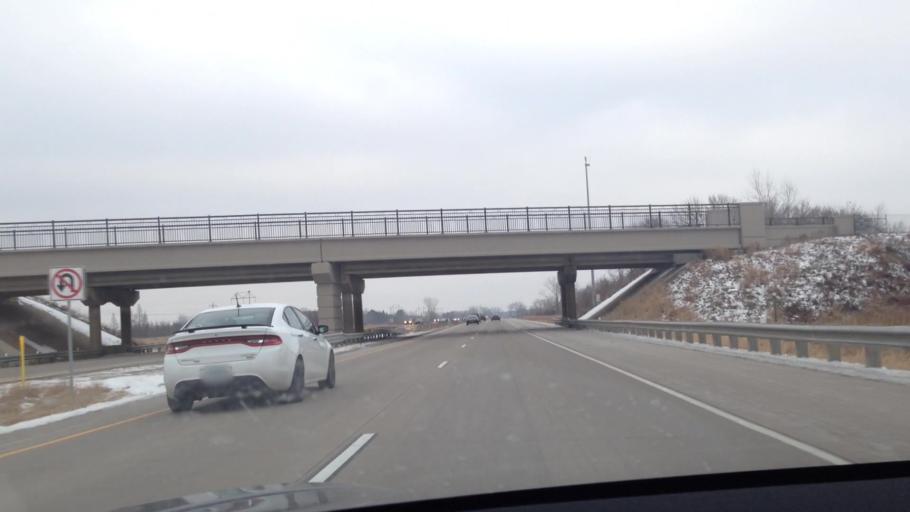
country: US
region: Minnesota
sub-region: Anoka County
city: Centerville
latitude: 45.1924
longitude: -93.0736
